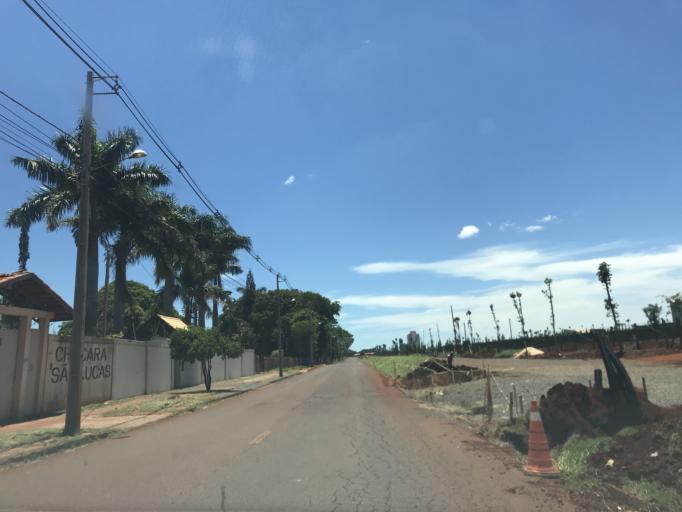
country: BR
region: Parana
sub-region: Sarandi
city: Sarandi
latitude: -23.4389
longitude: -51.8995
